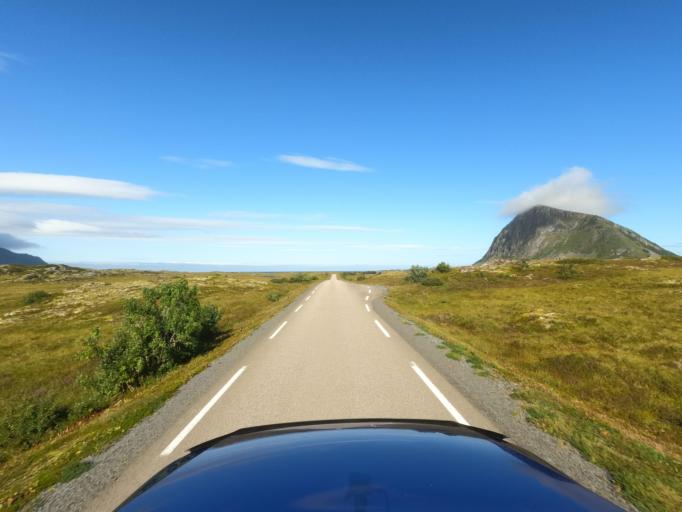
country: NO
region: Nordland
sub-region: Vestvagoy
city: Evjen
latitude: 68.3123
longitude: 14.0945
